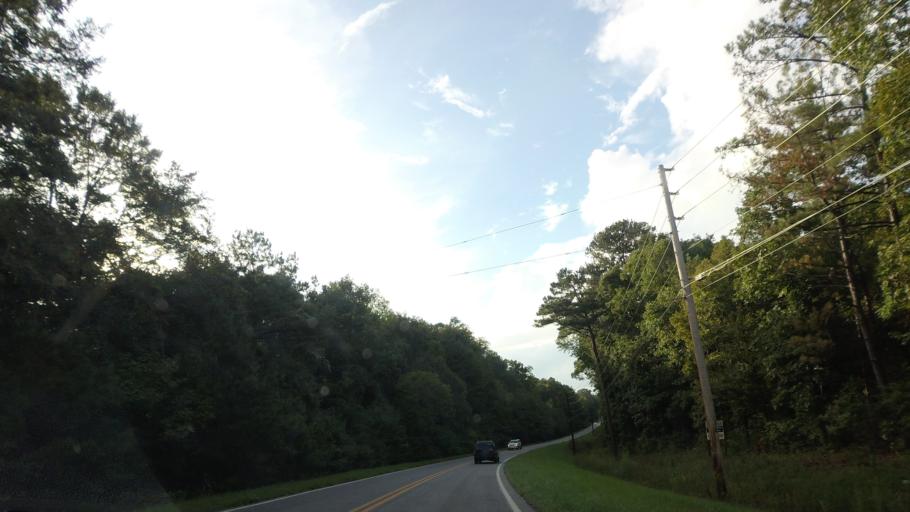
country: US
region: Georgia
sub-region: Bibb County
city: West Point
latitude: 32.8584
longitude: -83.7480
